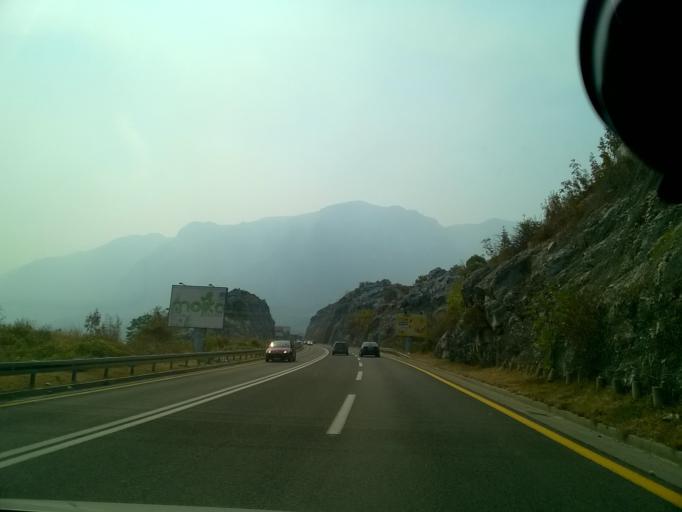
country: ME
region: Bar
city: Sutomore
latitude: 42.2104
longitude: 19.0480
